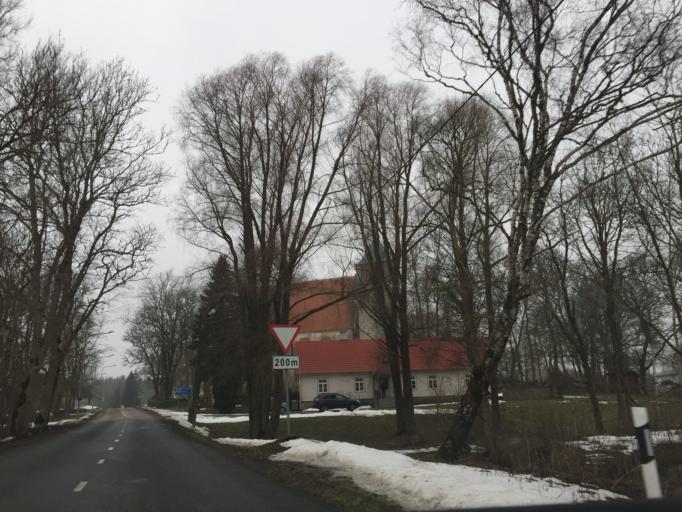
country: EE
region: Saare
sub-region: Kuressaare linn
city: Kuressaare
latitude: 58.4072
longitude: 22.7901
